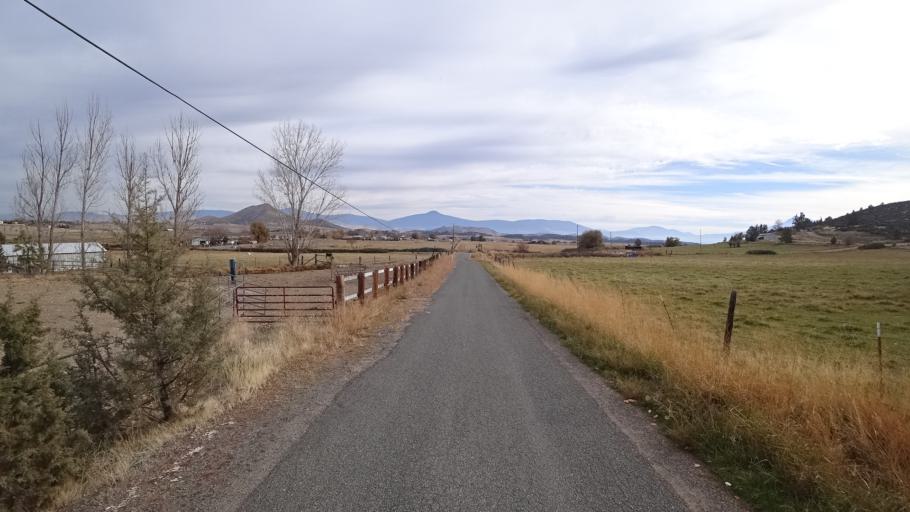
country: US
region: California
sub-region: Siskiyou County
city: Montague
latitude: 41.6983
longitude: -122.5512
